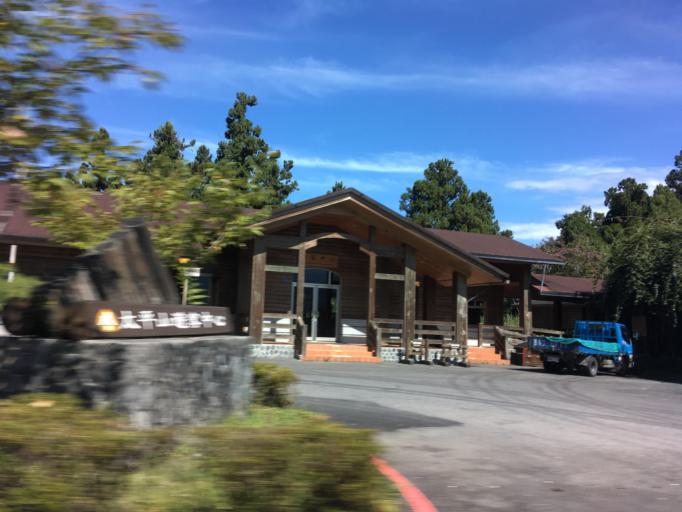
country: TW
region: Taiwan
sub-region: Yilan
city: Yilan
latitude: 24.5419
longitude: 121.5132
